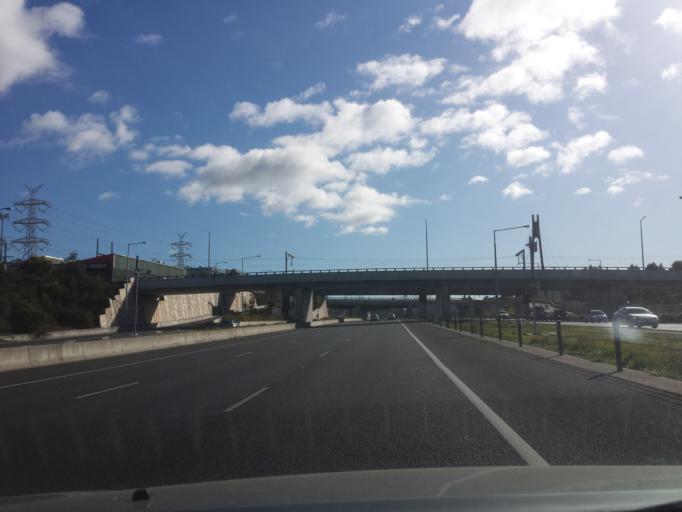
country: AU
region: Victoria
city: Mitcham
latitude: -37.8202
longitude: 145.2171
